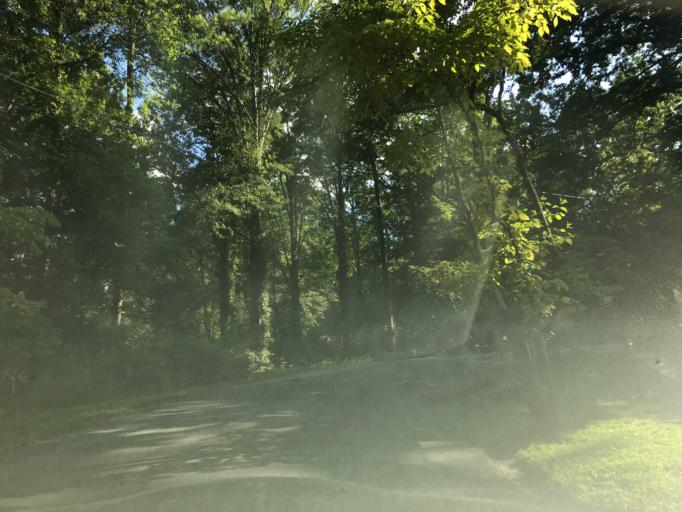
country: US
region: North Carolina
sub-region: Orange County
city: Chapel Hill
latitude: 35.9206
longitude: -79.0437
